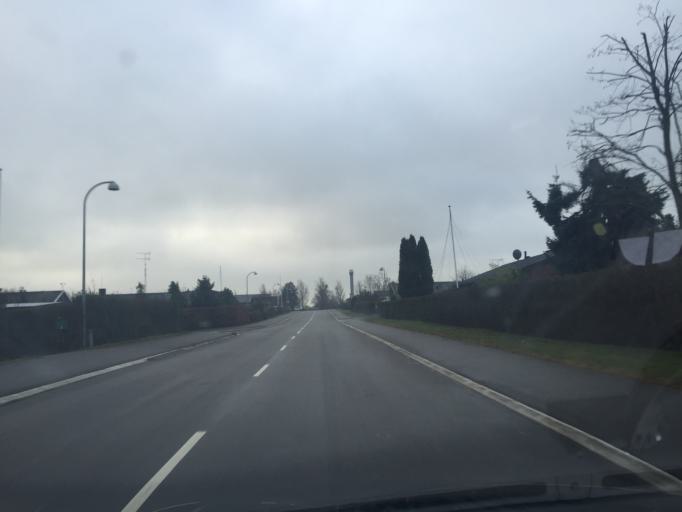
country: DK
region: Capital Region
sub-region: Hoje-Taastrup Kommune
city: Flong
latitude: 55.6820
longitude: 12.2390
